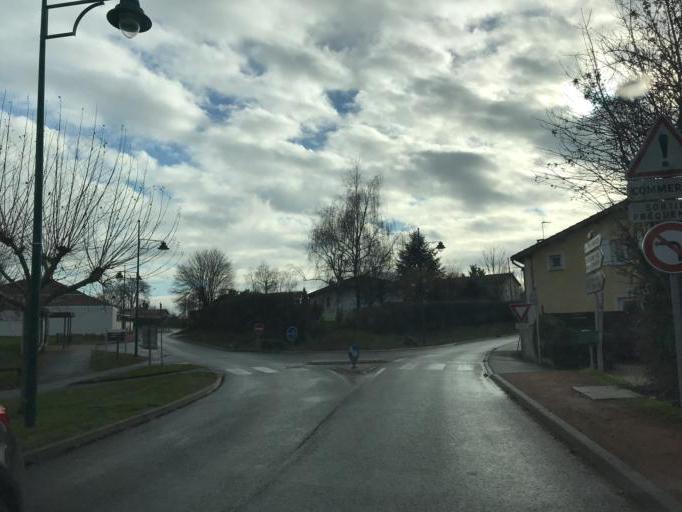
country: FR
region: Rhone-Alpes
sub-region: Departement de l'Ain
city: Sainte-Euphemie
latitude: 45.9711
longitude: 4.7993
